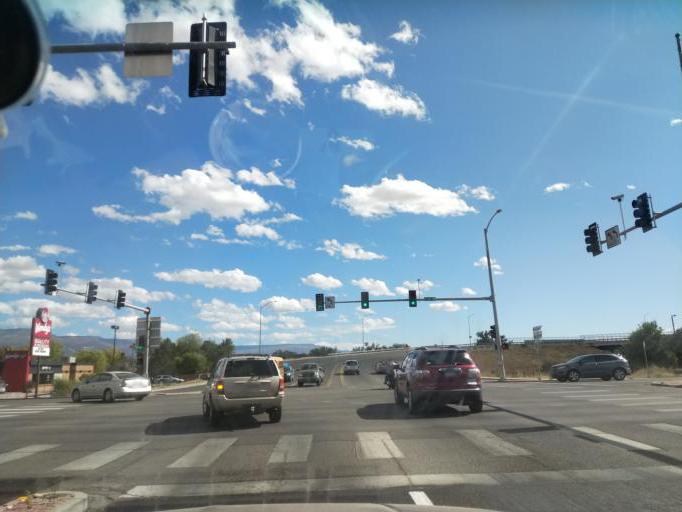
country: US
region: Colorado
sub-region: Mesa County
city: Clifton
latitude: 39.0881
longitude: -108.4582
